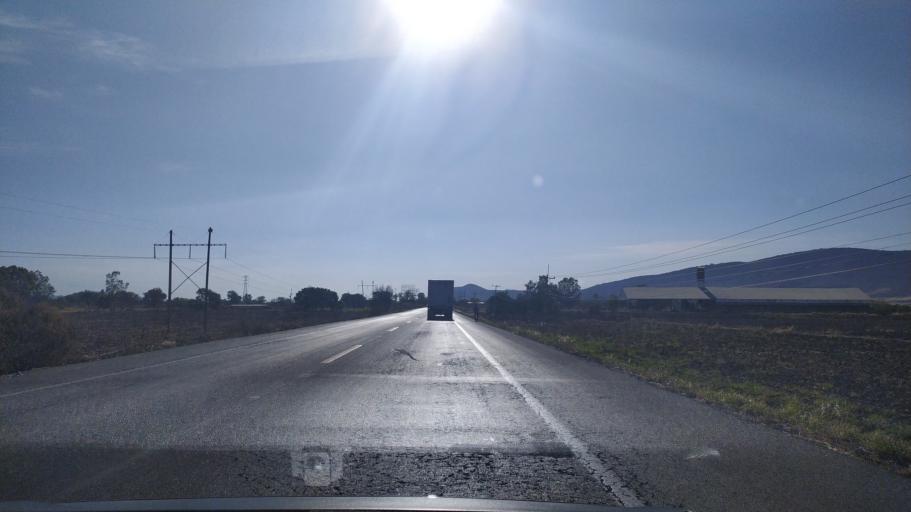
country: MX
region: Jalisco
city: Jamay
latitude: 20.2937
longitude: -102.6500
